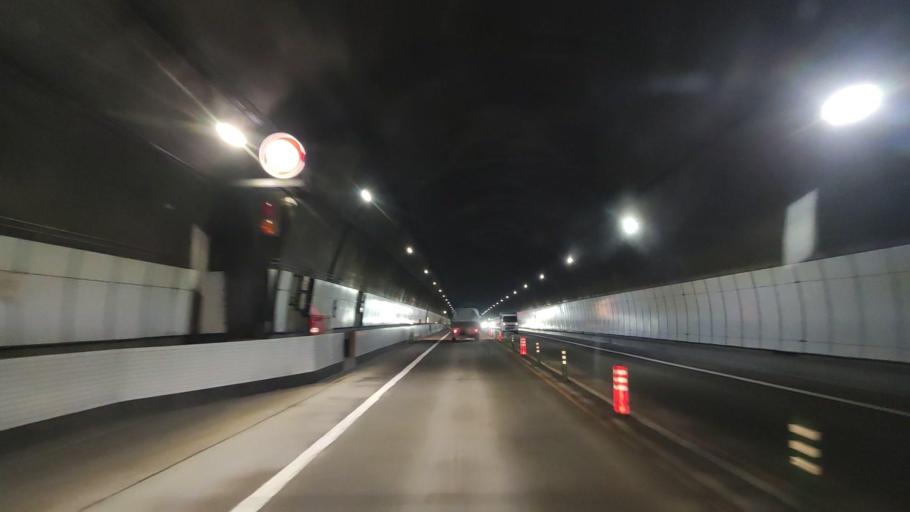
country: JP
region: Nagano
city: Hotaka
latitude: 36.1963
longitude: 137.5879
